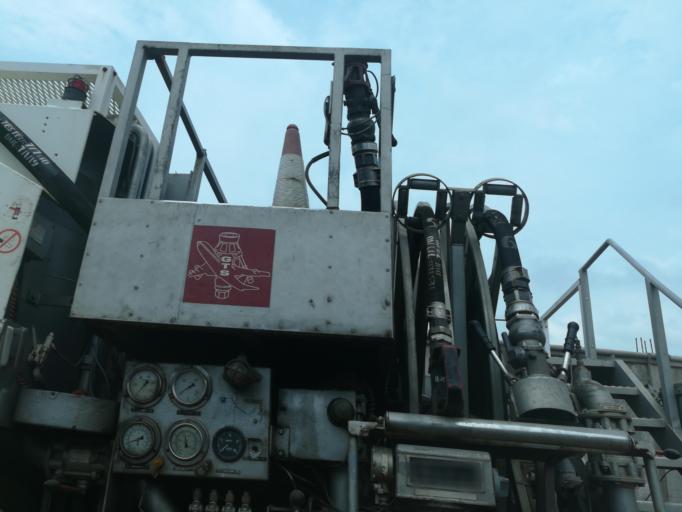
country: NG
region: Lagos
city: Oshodi
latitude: 6.5638
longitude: 3.3220
